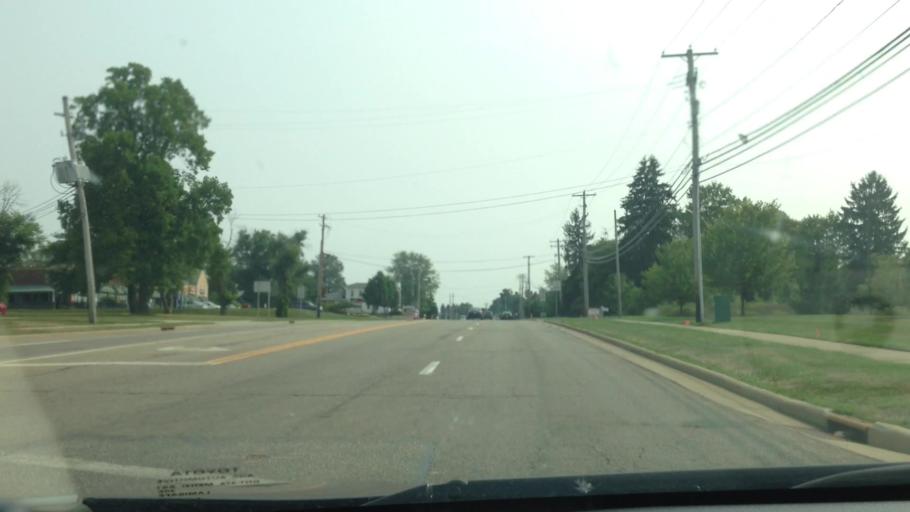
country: US
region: Ohio
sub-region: Summit County
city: Green
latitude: 40.9555
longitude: -81.4657
